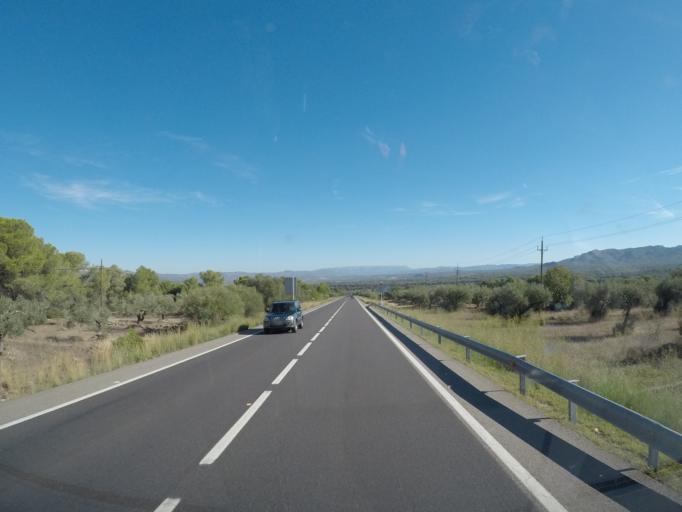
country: ES
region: Catalonia
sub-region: Provincia de Tarragona
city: Rasquera
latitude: 41.0095
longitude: 0.6075
